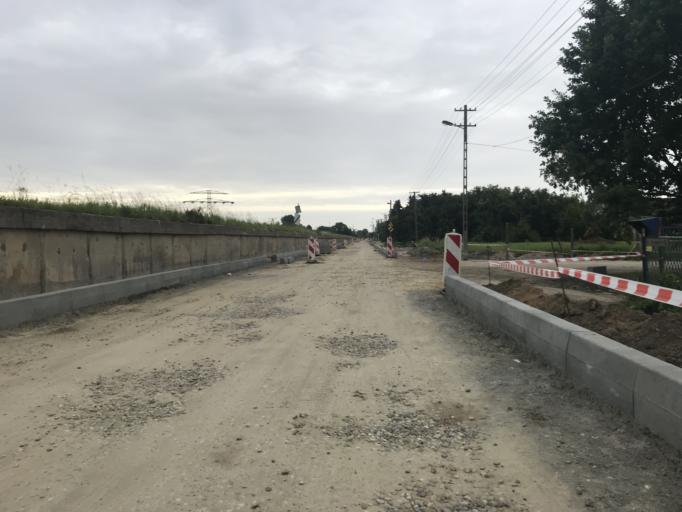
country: PL
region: Pomeranian Voivodeship
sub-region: Gdansk
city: Gdansk
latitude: 54.3436
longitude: 18.6822
